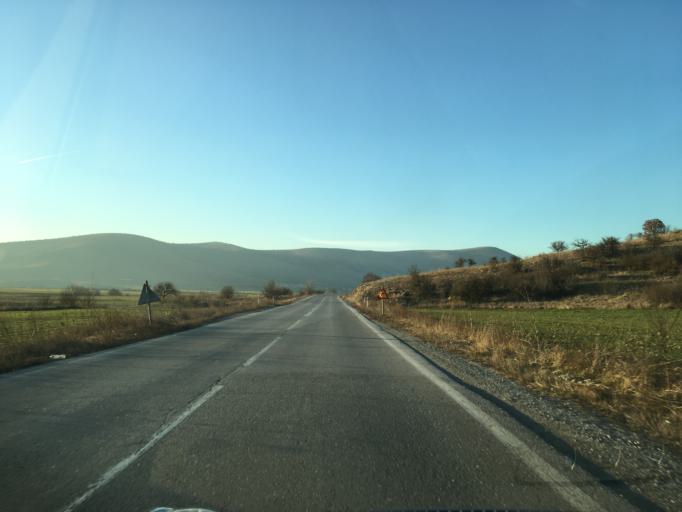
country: GR
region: West Macedonia
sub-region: Nomos Kozanis
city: Kozani
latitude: 40.3088
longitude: 21.7339
